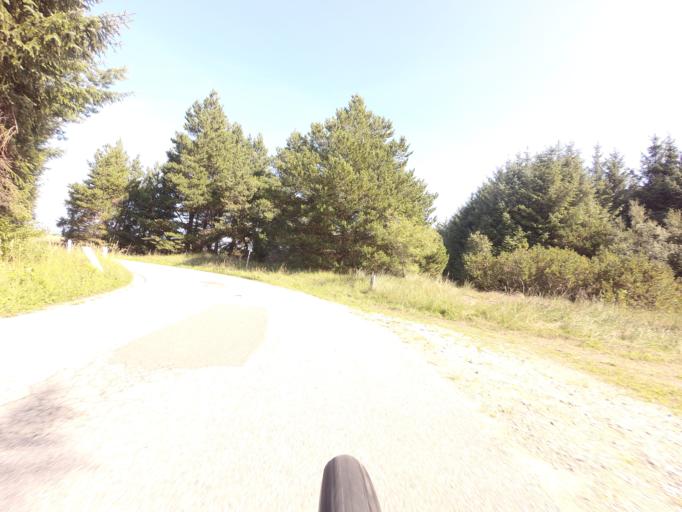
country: DK
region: North Denmark
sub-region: Hjorring Kommune
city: Hirtshals
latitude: 57.5820
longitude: 10.0361
